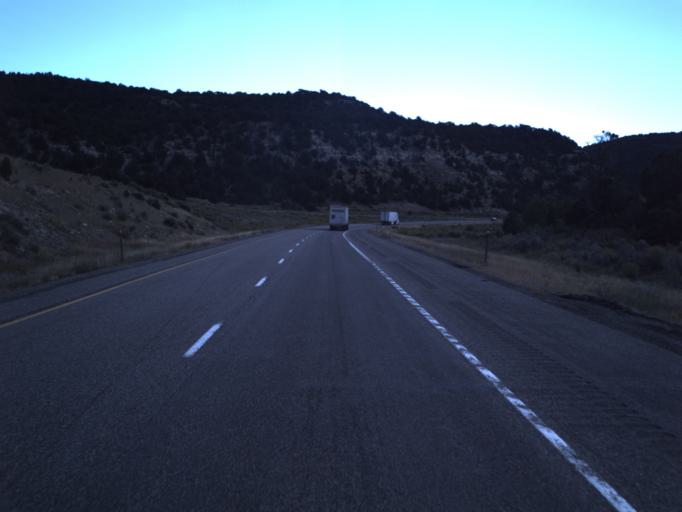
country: US
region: Utah
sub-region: Sevier County
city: Salina
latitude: 38.8514
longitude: -111.5454
